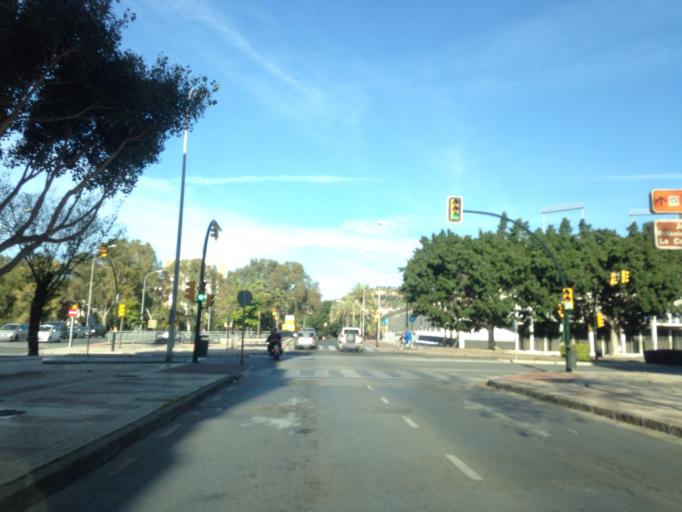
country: ES
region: Andalusia
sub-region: Provincia de Malaga
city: Malaga
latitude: 36.7329
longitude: -4.4246
